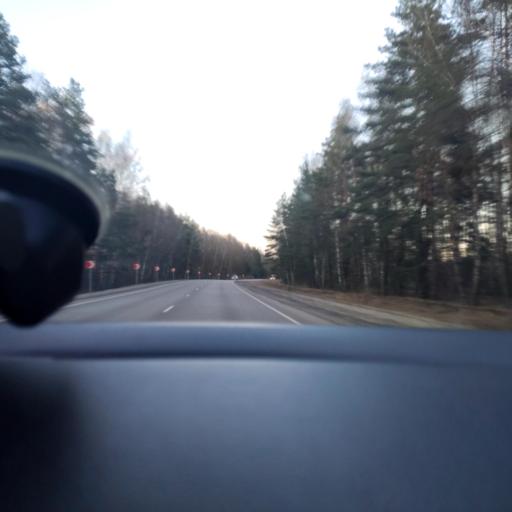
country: RU
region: Moskovskaya
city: Krasnyy Tkach
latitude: 55.4015
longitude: 39.1347
